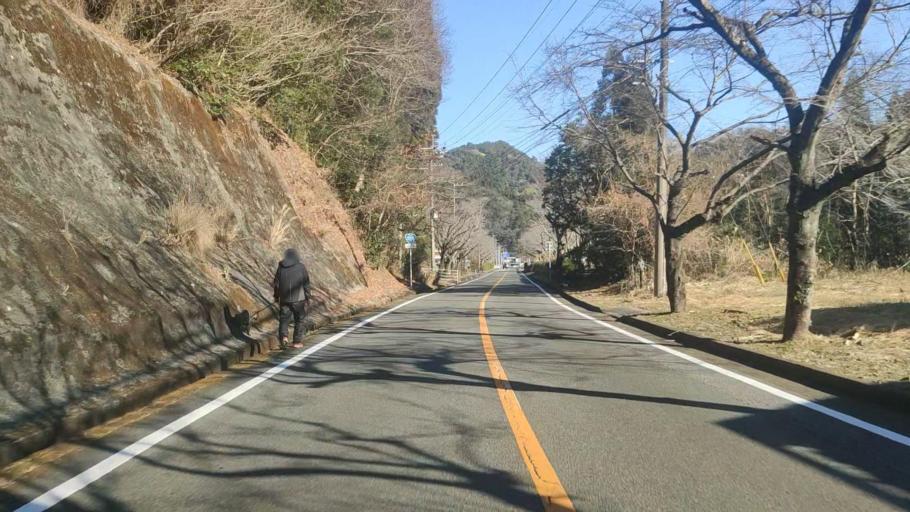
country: JP
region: Miyazaki
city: Nobeoka
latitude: 32.6415
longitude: 131.7445
